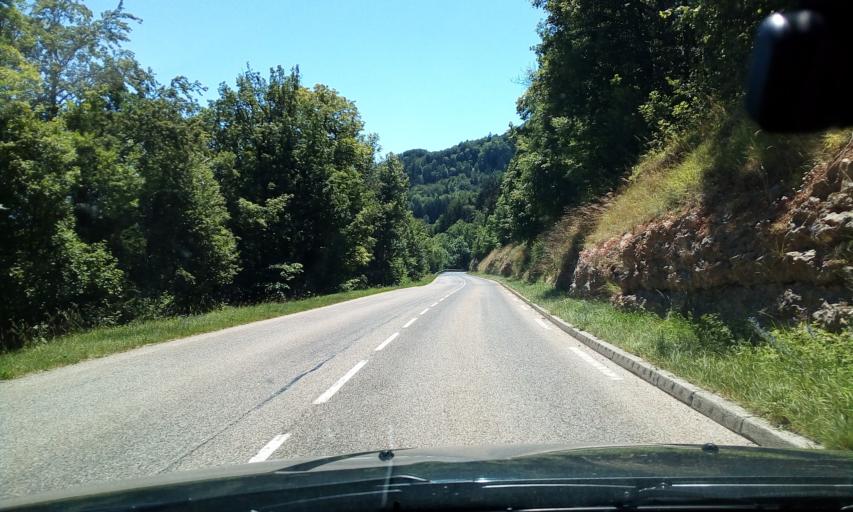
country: FR
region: Rhone-Alpes
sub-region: Departement de l'Isere
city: Sassenage
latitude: 45.1745
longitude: 5.6480
